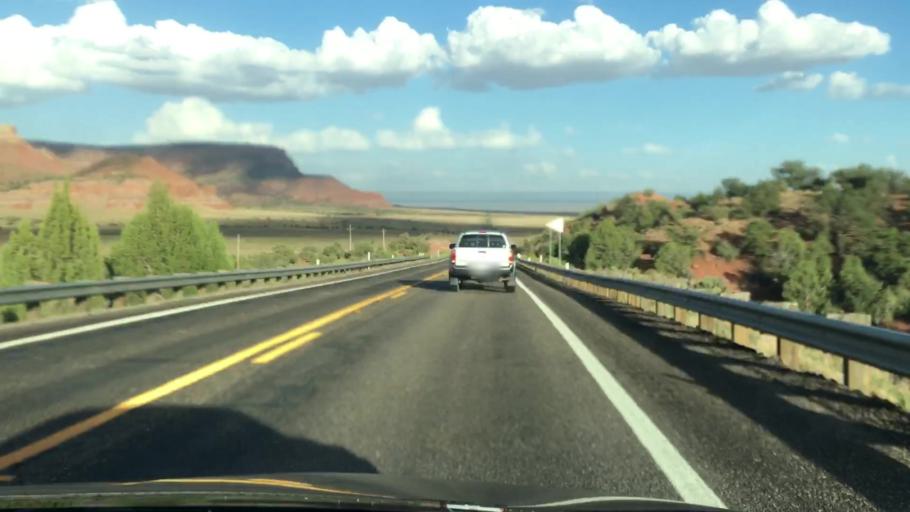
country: US
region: Arizona
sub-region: Mohave County
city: Colorado City
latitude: 36.8802
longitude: -112.8929
